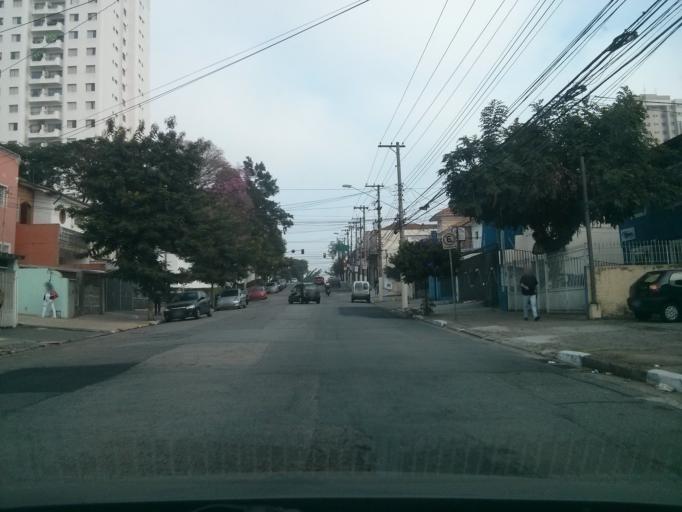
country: BR
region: Sao Paulo
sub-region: Sao Paulo
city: Sao Paulo
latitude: -23.6041
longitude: -46.6338
